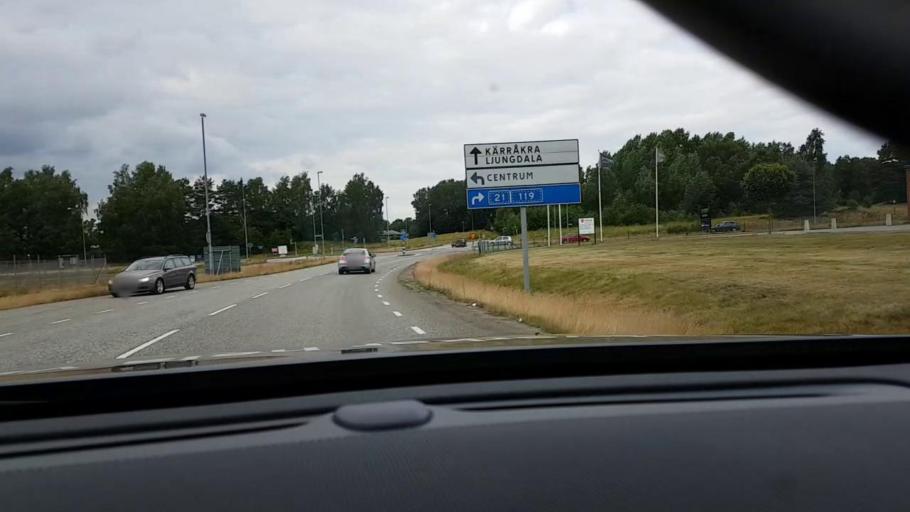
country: SE
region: Skane
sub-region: Hassleholms Kommun
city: Hassleholm
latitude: 56.1683
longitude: 13.8020
